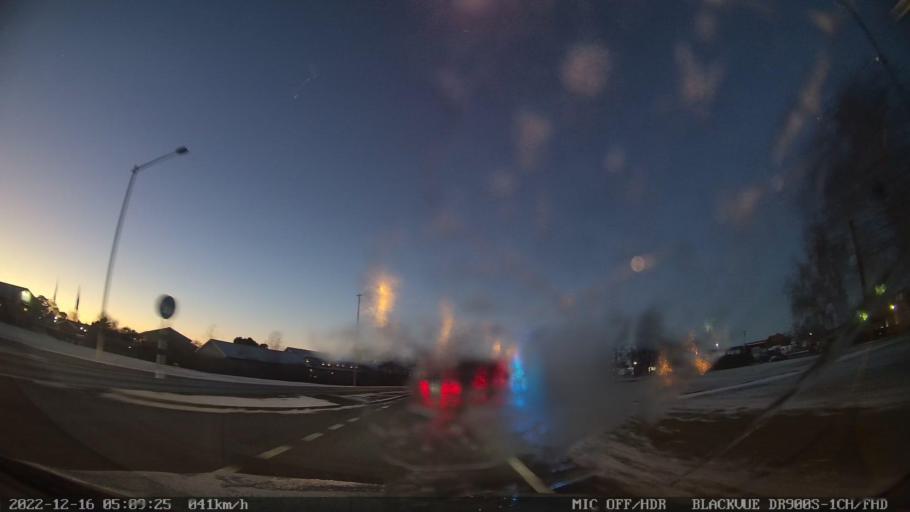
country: SE
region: Skane
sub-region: Tomelilla Kommun
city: Tomelilla
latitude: 55.5453
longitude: 13.9681
